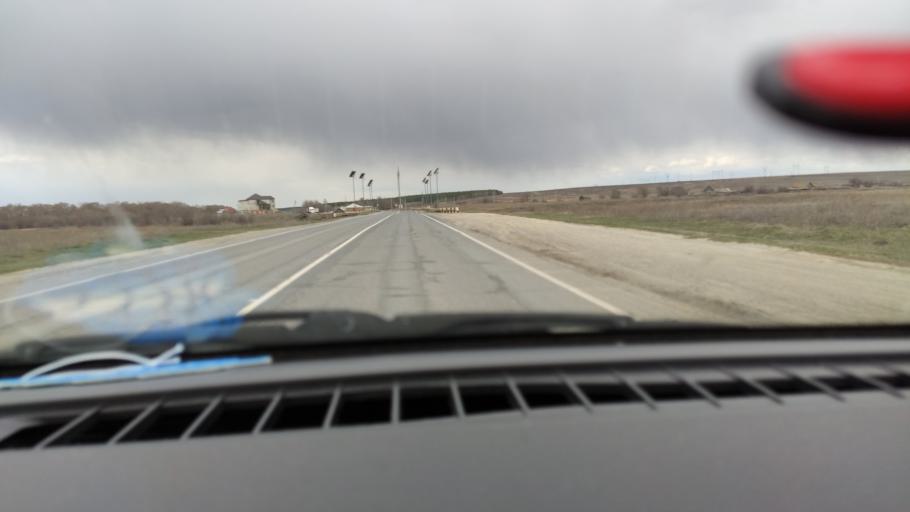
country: RU
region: Saratov
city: Sinodskoye
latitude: 52.0487
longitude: 46.7465
